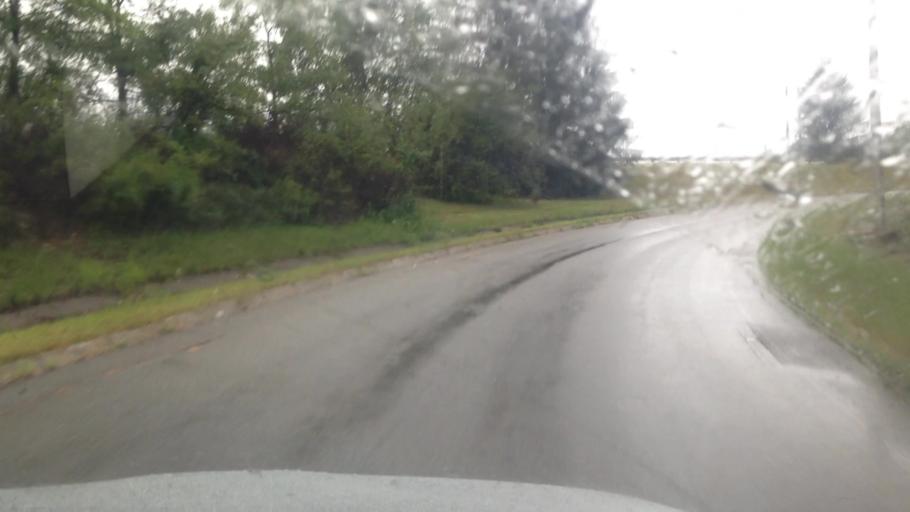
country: US
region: Massachusetts
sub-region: Worcester County
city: Auburn
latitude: 42.1829
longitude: -71.8491
